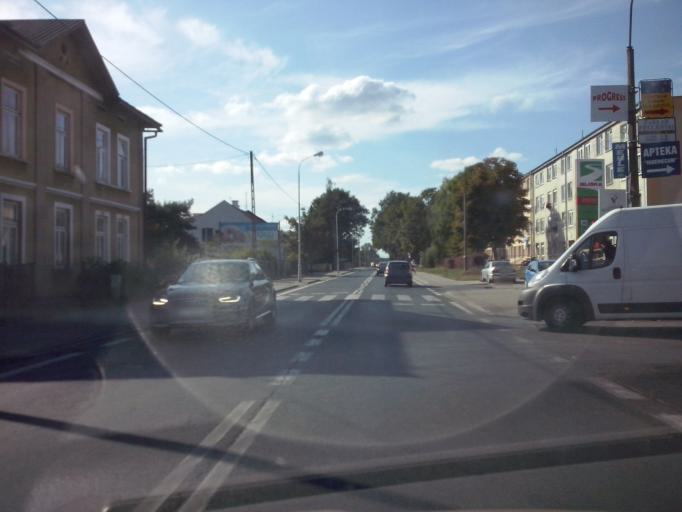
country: PL
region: Subcarpathian Voivodeship
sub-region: Powiat nizanski
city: Nisko
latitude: 50.5221
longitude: 22.1327
